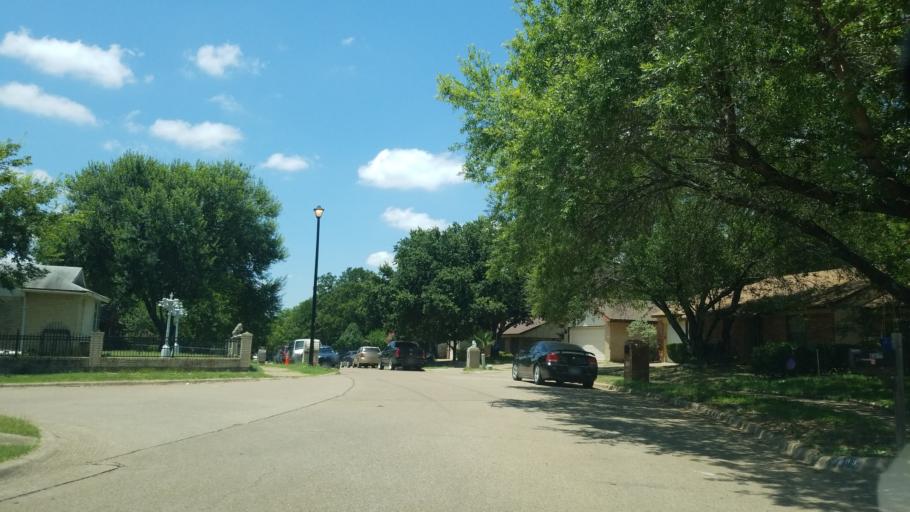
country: US
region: Texas
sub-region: Dallas County
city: Balch Springs
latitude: 32.7430
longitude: -96.7042
